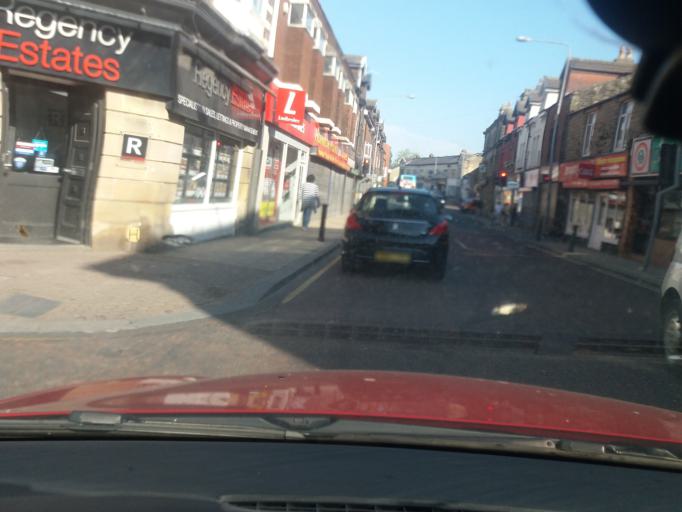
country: GB
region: England
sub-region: Borough of Bolton
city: Horwich
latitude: 53.5997
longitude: -2.5460
